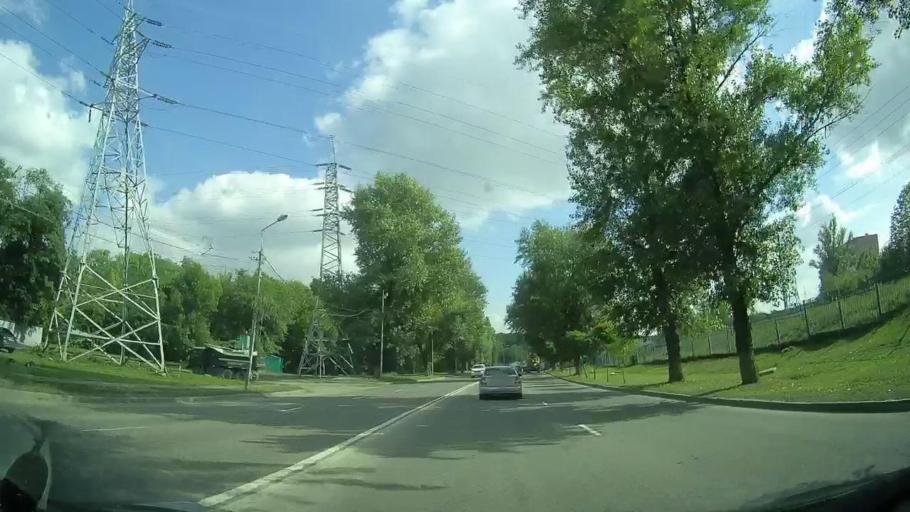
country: RU
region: Rostov
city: Imeni Chkalova
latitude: 47.2591
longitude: 39.7906
